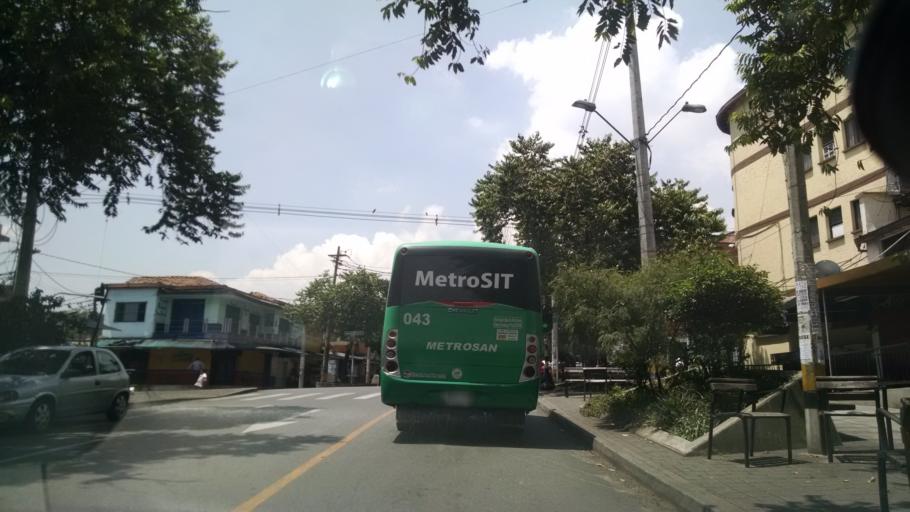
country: CO
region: Antioquia
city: Medellin
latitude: 6.2569
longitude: -75.6149
